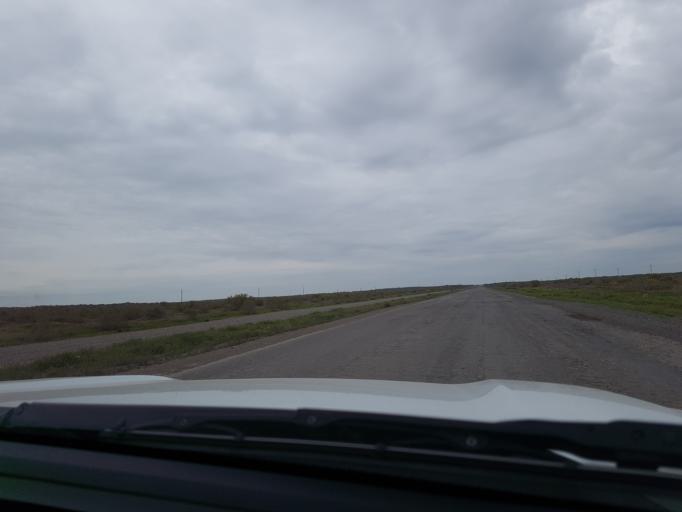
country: TM
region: Mary
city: Bayramaly
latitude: 37.9258
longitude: 62.6251
